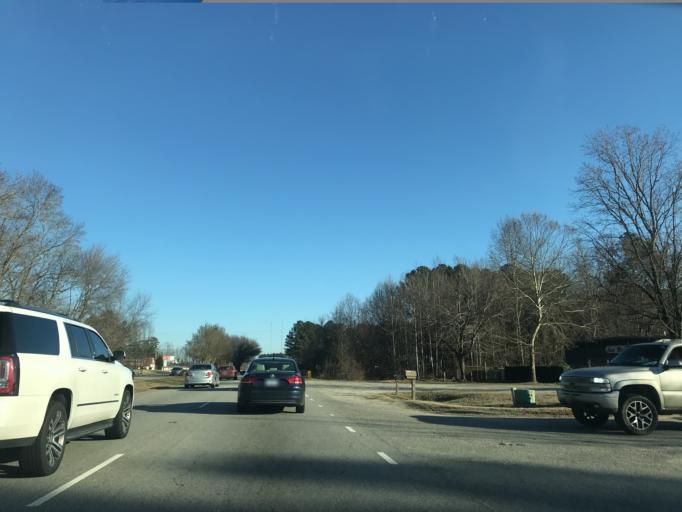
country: US
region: North Carolina
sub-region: Wake County
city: Garner
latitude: 35.7015
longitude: -78.6002
